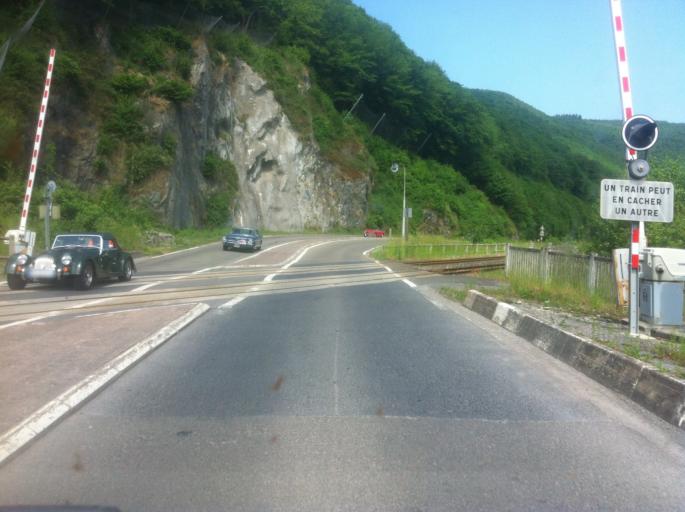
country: FR
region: Champagne-Ardenne
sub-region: Departement des Ardennes
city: Haybes
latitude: 49.9961
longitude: 4.6957
